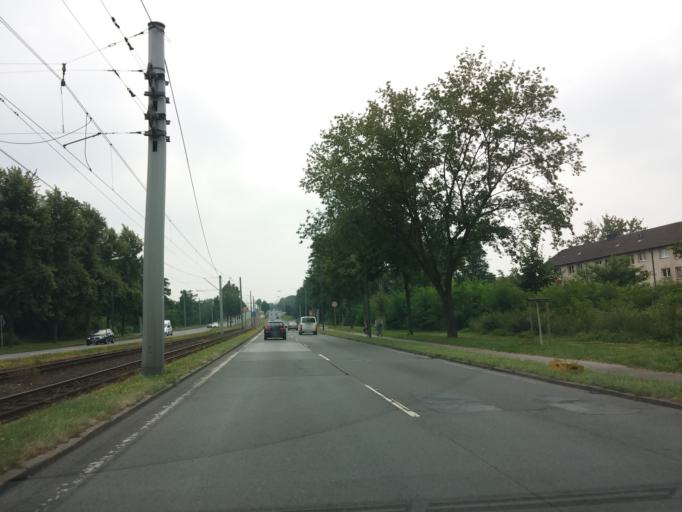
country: DE
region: North Rhine-Westphalia
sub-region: Regierungsbezirk Munster
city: Gelsenkirchen
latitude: 51.5456
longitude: 7.0671
